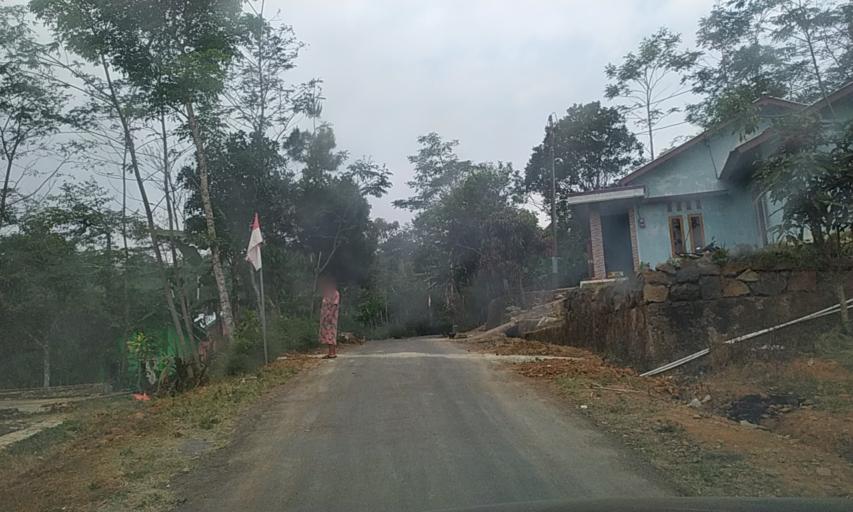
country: ID
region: Central Java
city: Randudongkal
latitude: -7.1859
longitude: 109.4203
